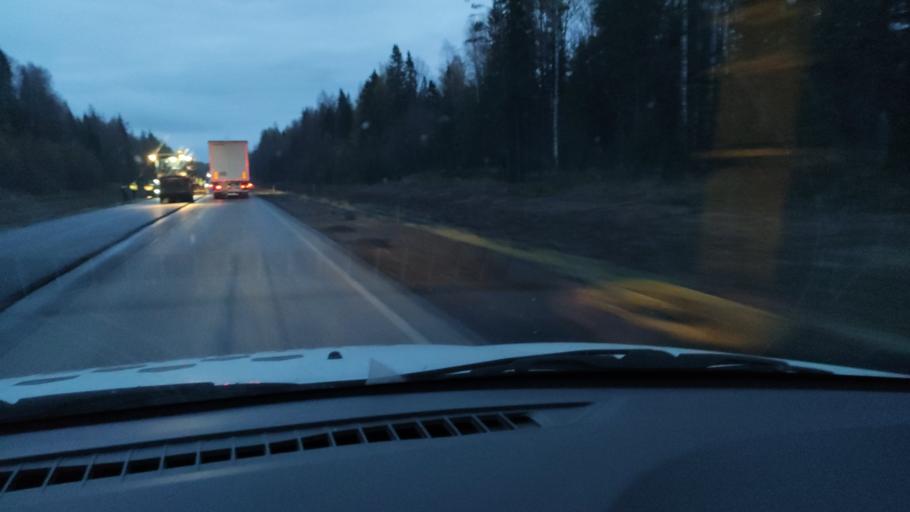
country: RU
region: Kirov
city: Kostino
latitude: 58.8247
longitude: 53.3701
